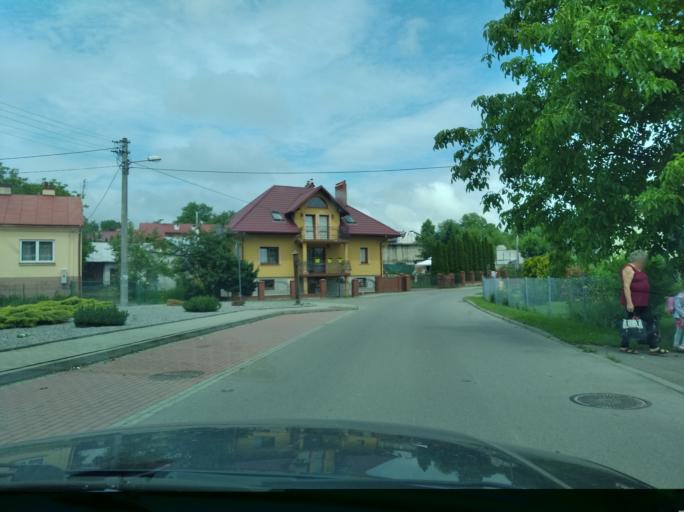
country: PL
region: Subcarpathian Voivodeship
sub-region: Powiat jaroslawski
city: Pruchnik
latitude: 49.9031
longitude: 22.5136
